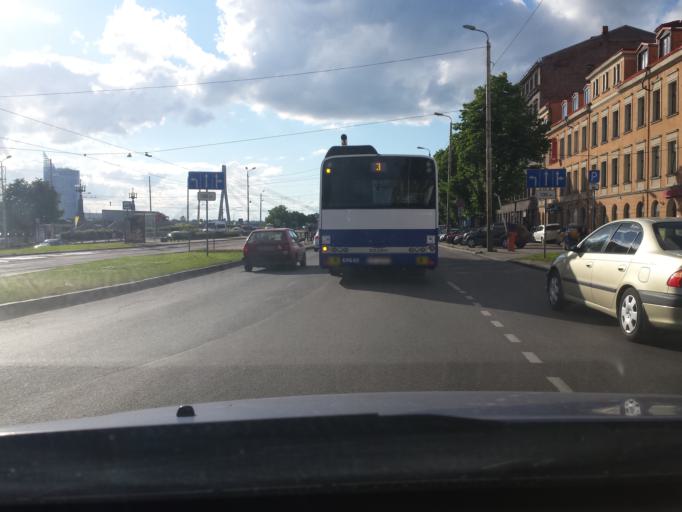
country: LV
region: Riga
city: Riga
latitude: 56.9455
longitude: 24.1069
